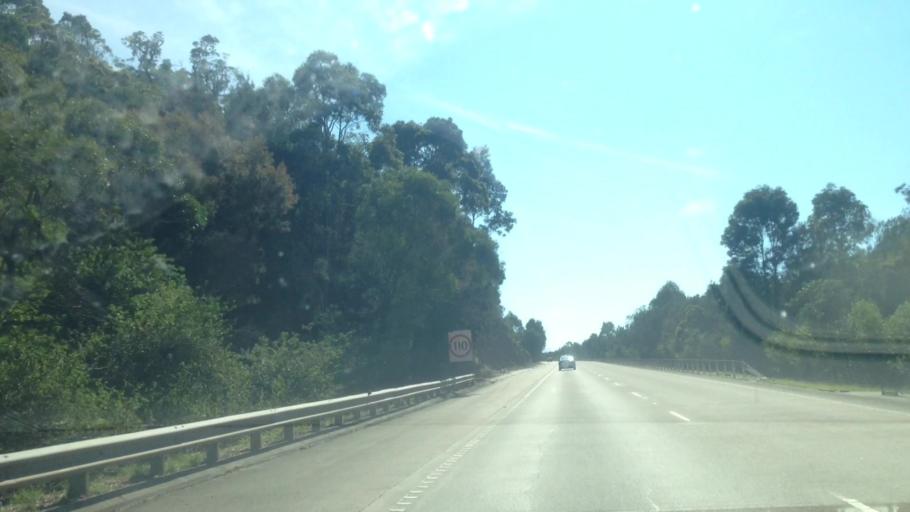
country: AU
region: New South Wales
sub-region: Lake Macquarie Shire
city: Toronto
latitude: -32.9814
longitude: 151.5243
